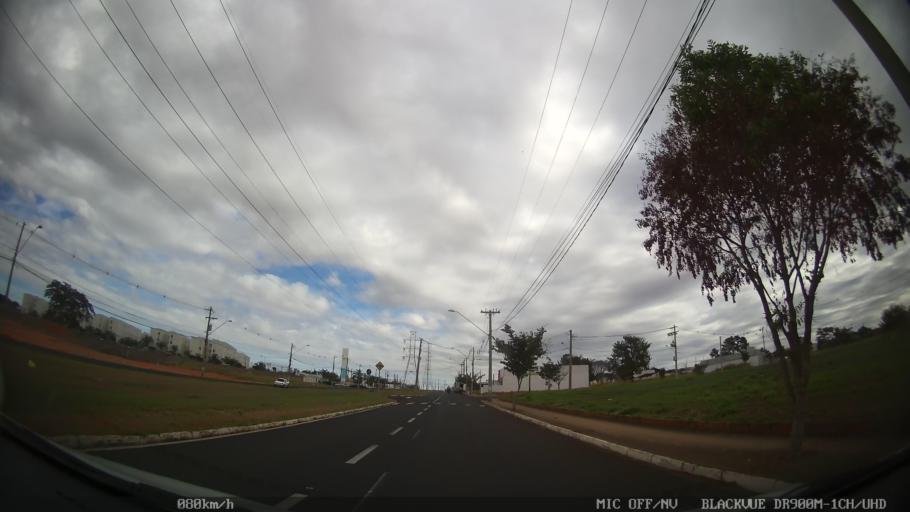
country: BR
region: Sao Paulo
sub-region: Sao Jose Do Rio Preto
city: Sao Jose do Rio Preto
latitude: -20.8163
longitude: -49.4883
